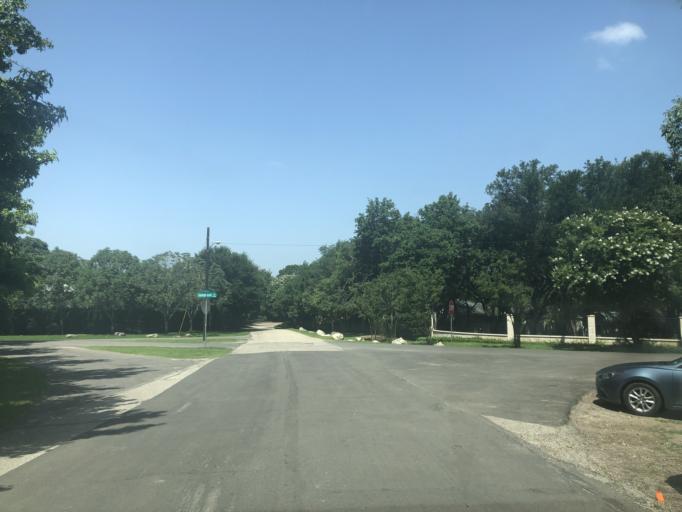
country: US
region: Texas
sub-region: Dallas County
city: University Park
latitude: 32.8697
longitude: -96.8264
